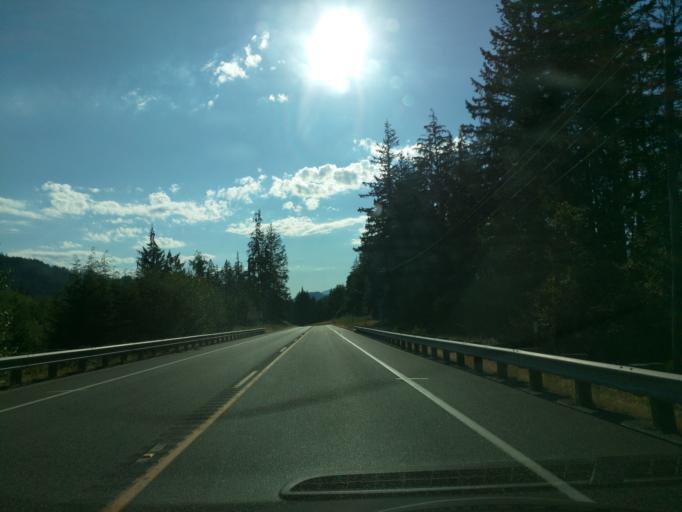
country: US
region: Washington
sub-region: Snohomish County
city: Darrington
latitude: 48.2787
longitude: -121.7684
